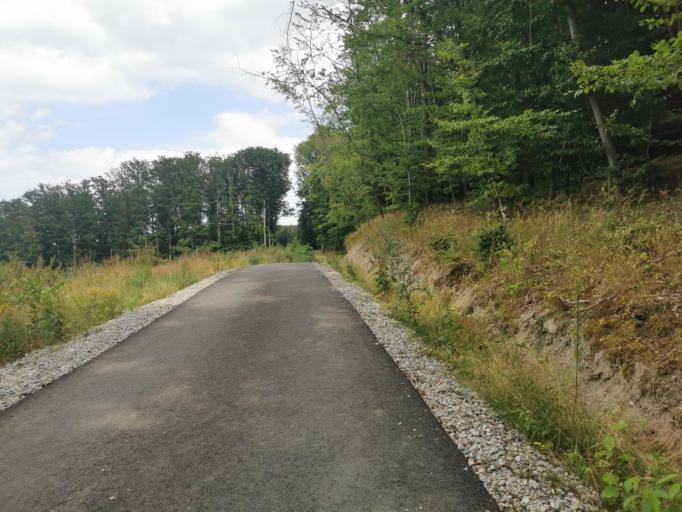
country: SK
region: Trenciansky
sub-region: Okres Myjava
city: Myjava
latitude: 48.7286
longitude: 17.5096
